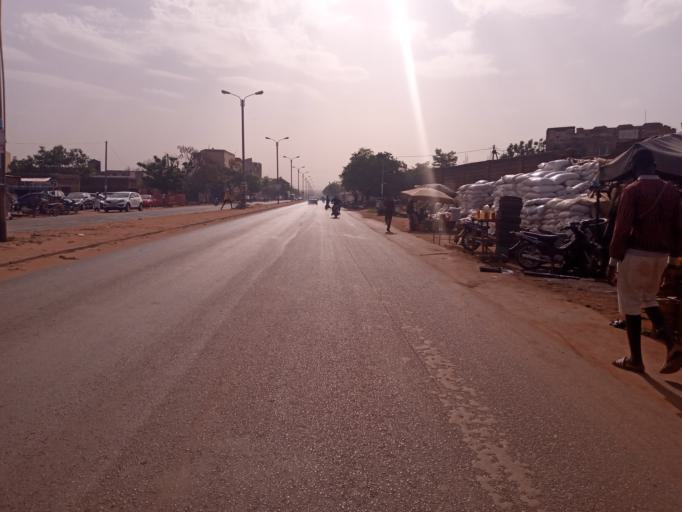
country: ML
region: Bamako
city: Bamako
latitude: 12.5768
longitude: -7.9509
